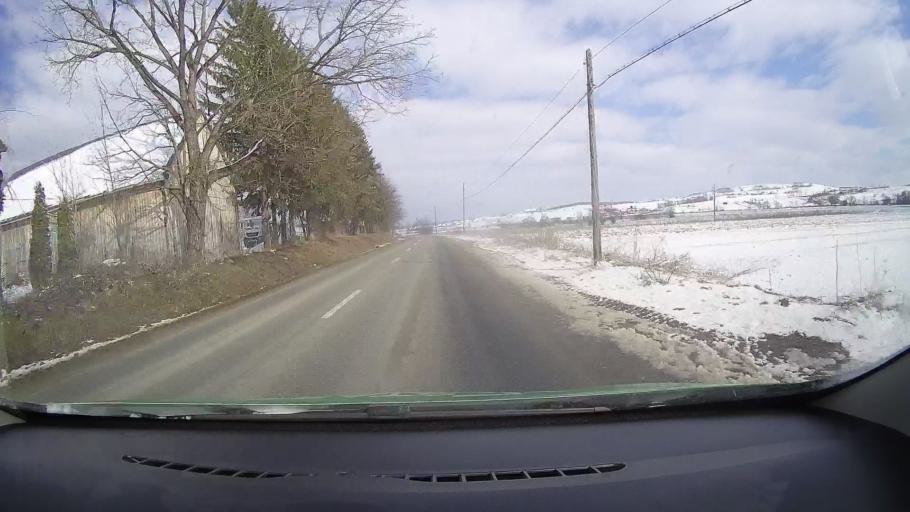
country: RO
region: Sibiu
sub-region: Oras Agnita
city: Agnita
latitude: 45.9658
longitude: 24.5993
